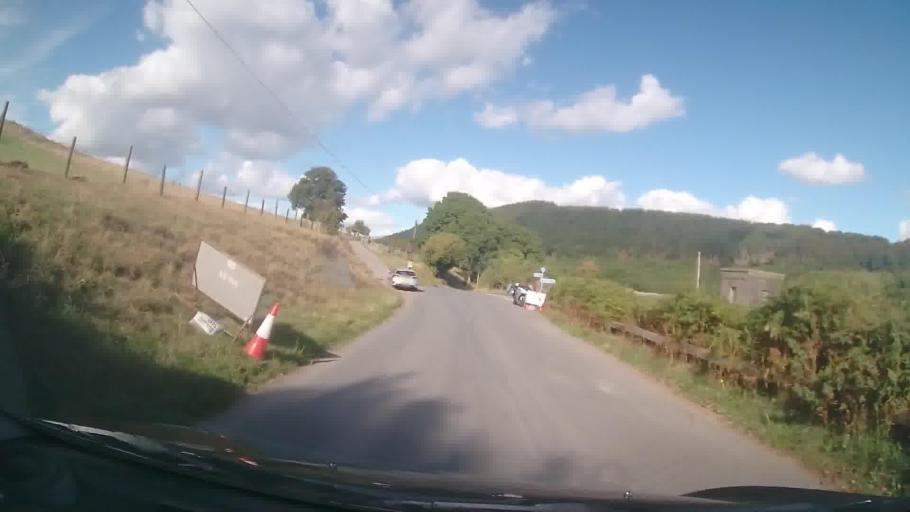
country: GB
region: Wales
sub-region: Sir Powys
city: Brecon
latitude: 51.8761
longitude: -3.3046
